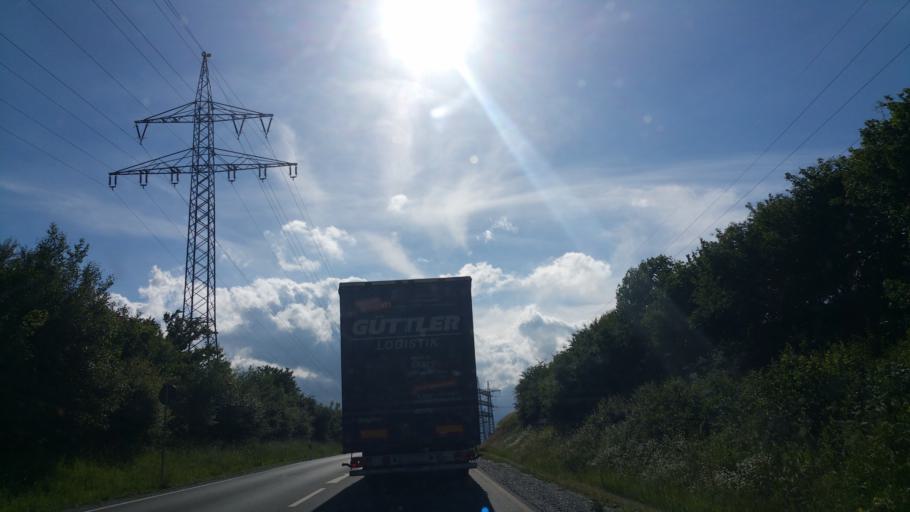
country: DE
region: Bavaria
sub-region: Upper Franconia
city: Schwarzenbach an der Saale
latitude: 50.2262
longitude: 11.9497
